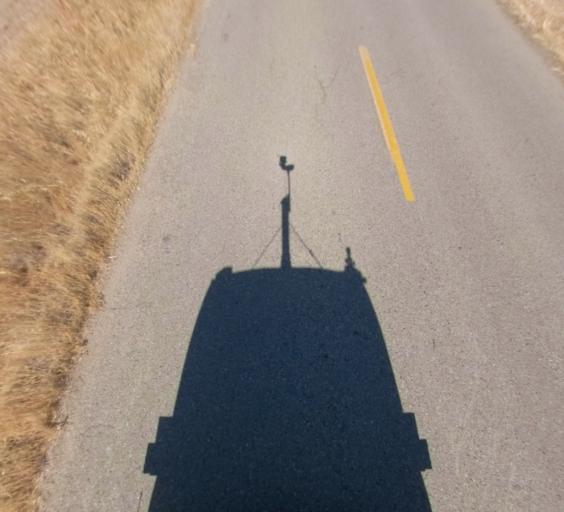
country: US
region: California
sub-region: Madera County
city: Bonadelle Ranchos-Madera Ranchos
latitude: 36.9813
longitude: -119.8742
